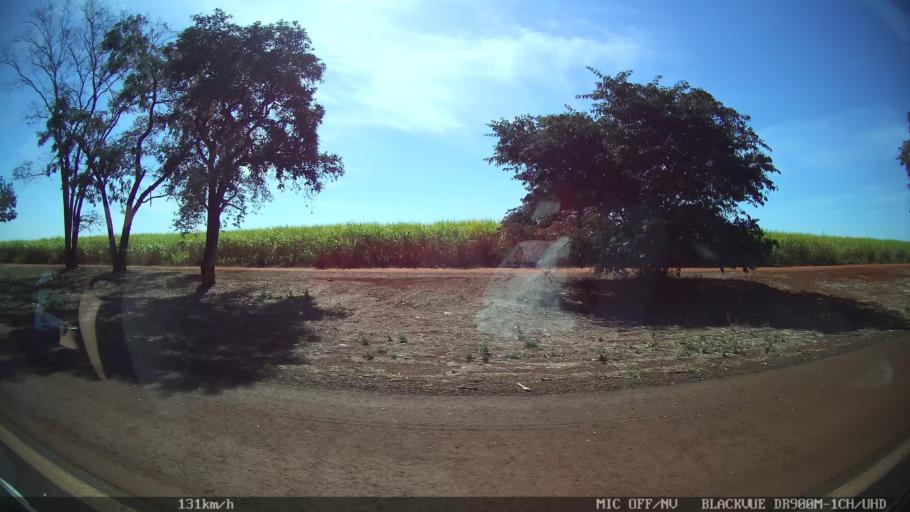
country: BR
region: Sao Paulo
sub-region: Guaira
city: Guaira
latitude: -20.4439
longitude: -48.3024
